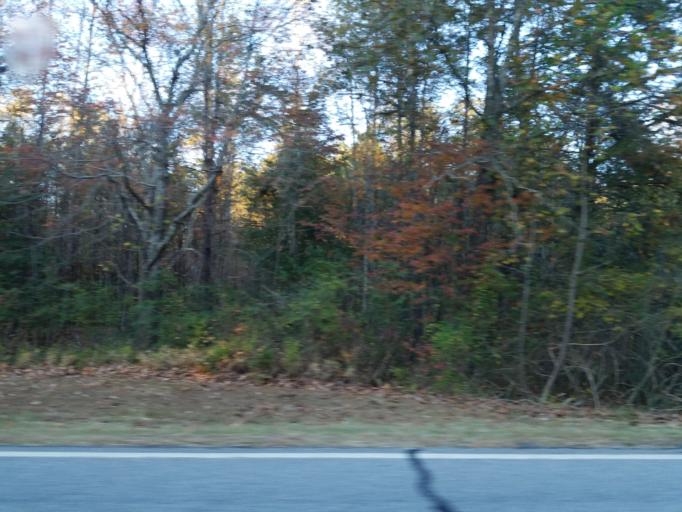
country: US
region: Georgia
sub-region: Lumpkin County
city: Dahlonega
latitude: 34.5213
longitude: -84.0470
